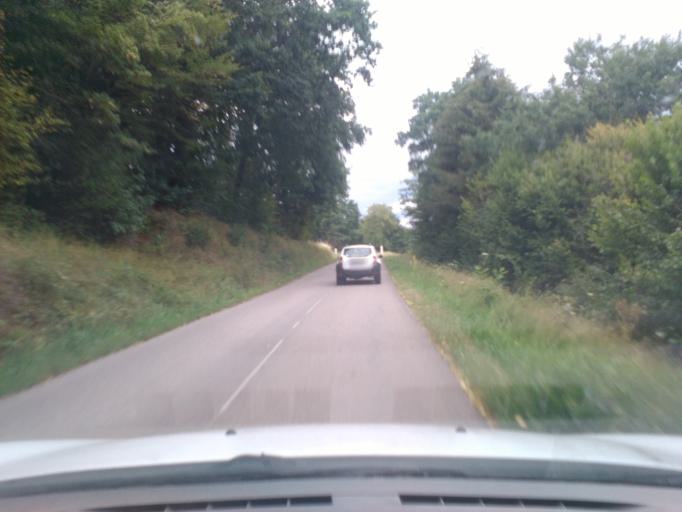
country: FR
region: Lorraine
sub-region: Departement des Vosges
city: Saint-Michel-sur-Meurthe
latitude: 48.3130
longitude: 6.8664
